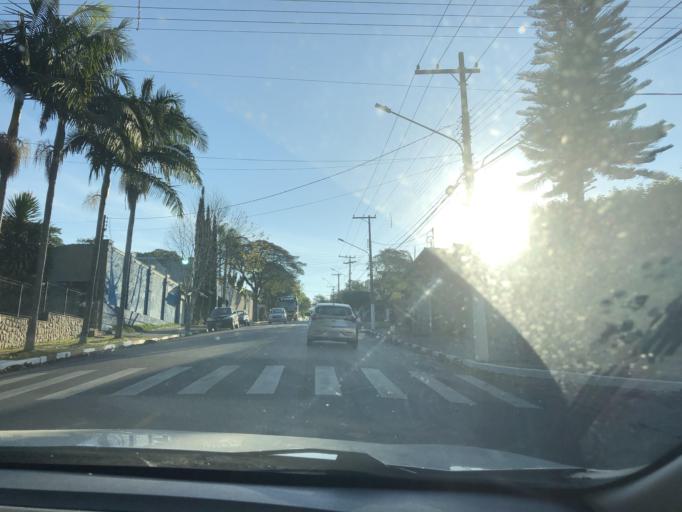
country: BR
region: Sao Paulo
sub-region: Atibaia
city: Atibaia
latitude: -23.1154
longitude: -46.5378
